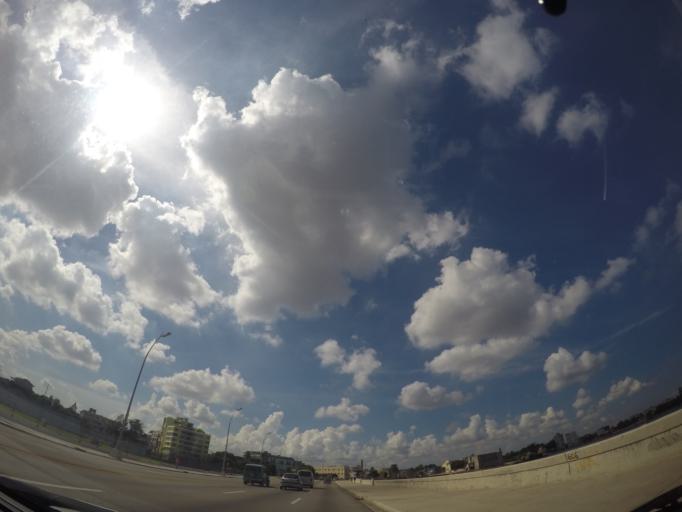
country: CU
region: La Habana
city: Havana
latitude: 23.1340
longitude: -82.4081
